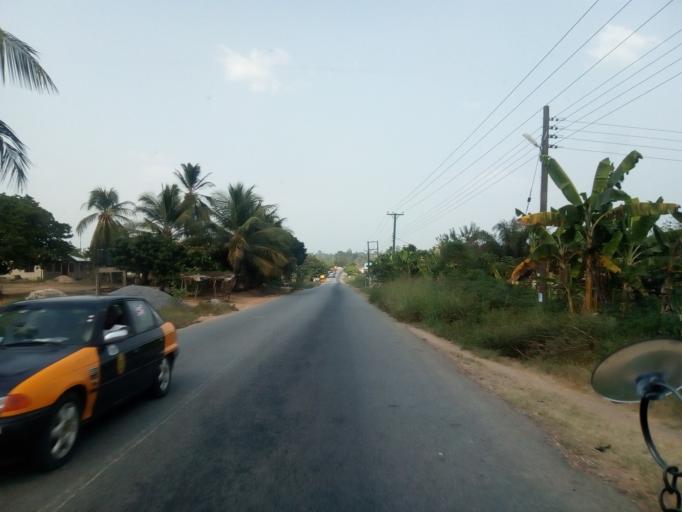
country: GH
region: Eastern
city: Suhum
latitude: 6.0600
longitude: -0.4018
